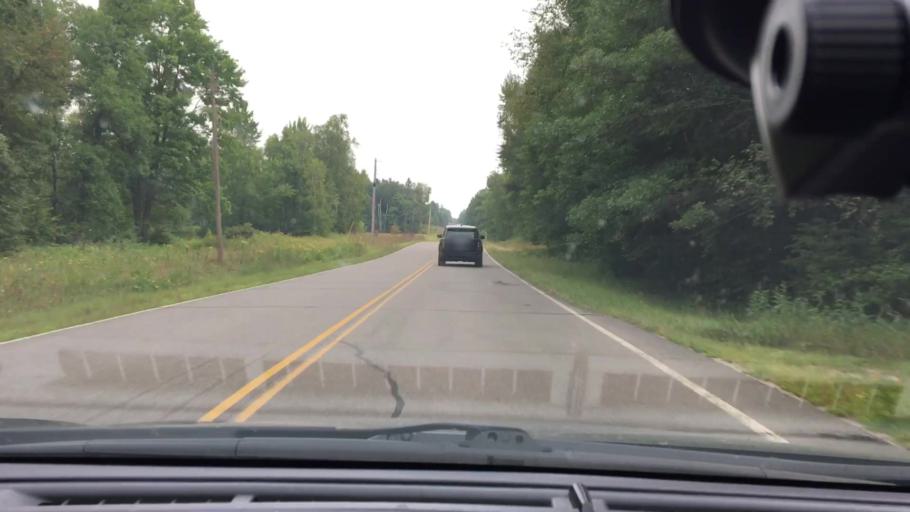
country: US
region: Minnesota
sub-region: Crow Wing County
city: Cross Lake
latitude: 46.6507
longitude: -94.0095
